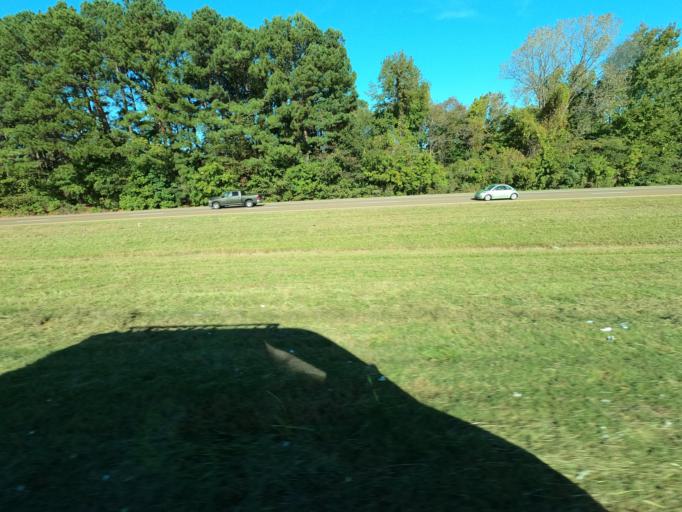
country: US
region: Tennessee
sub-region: Tipton County
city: Munford
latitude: 35.4067
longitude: -89.8373
